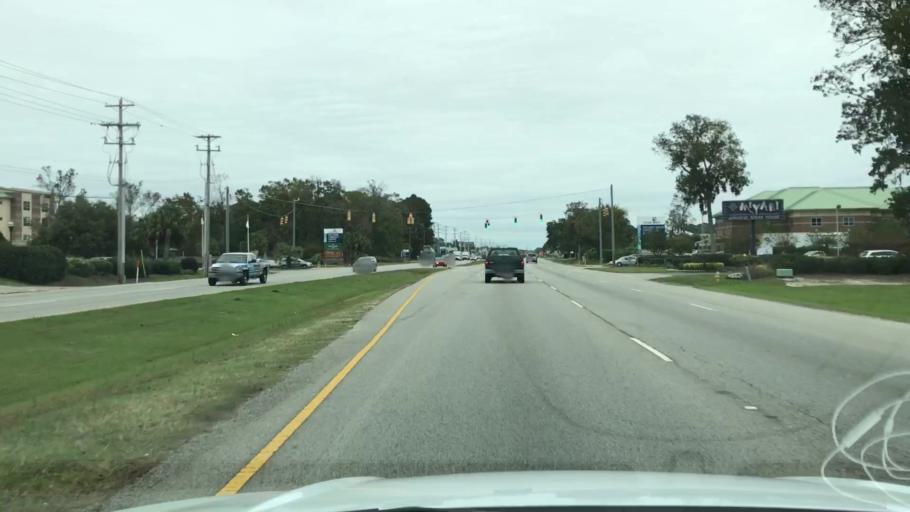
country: US
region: South Carolina
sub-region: Georgetown County
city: Murrells Inlet
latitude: 33.5580
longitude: -79.0425
